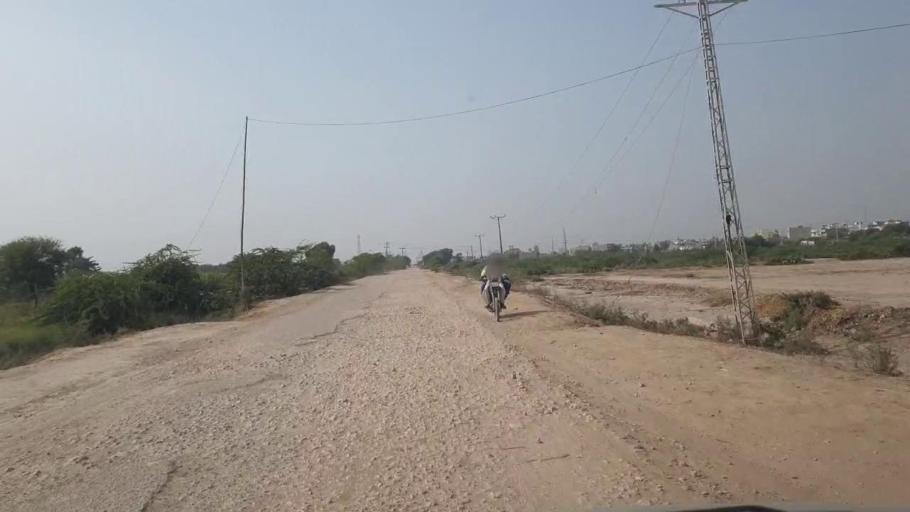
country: PK
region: Sindh
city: Matli
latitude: 25.0312
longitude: 68.6630
